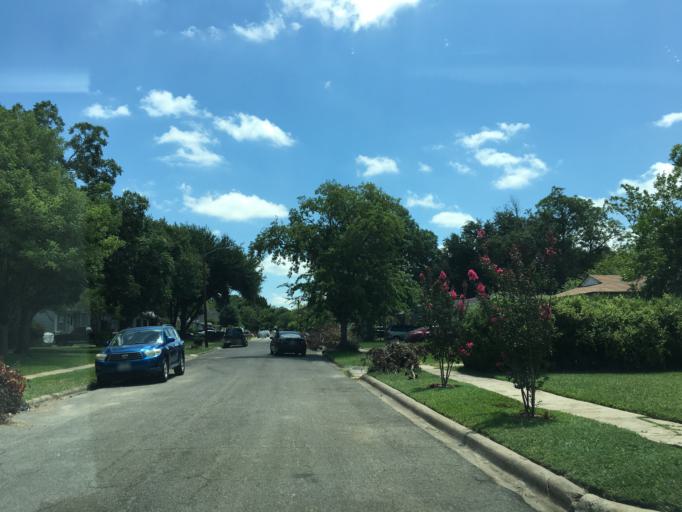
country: US
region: Texas
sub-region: Dallas County
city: Garland
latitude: 32.8402
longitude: -96.6726
